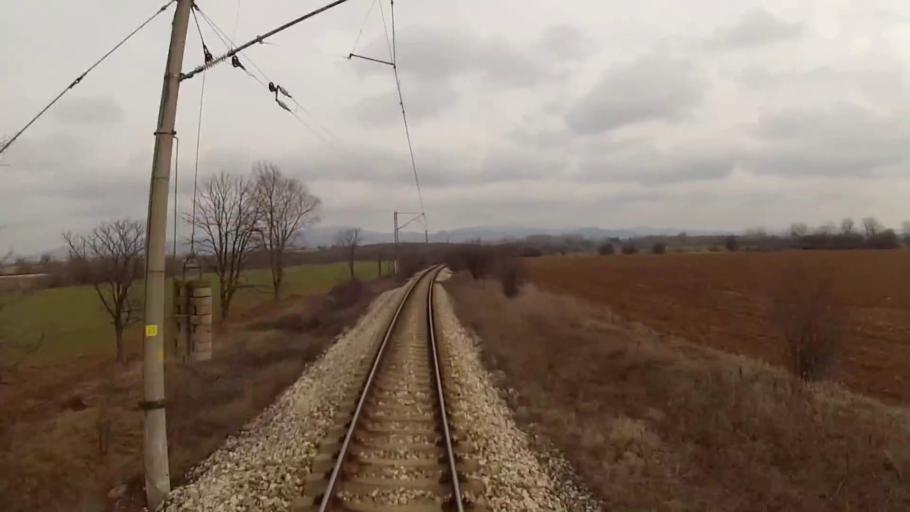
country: BG
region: Sofiya
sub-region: Obshtina Elin Pelin
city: Elin Pelin
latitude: 42.7140
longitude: 23.5807
